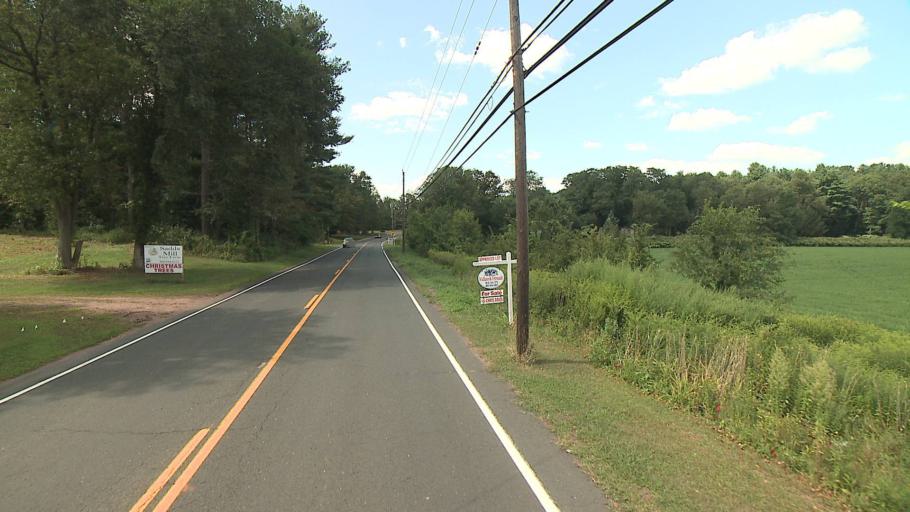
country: US
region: Connecticut
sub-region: Tolland County
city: Ellington
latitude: 41.9076
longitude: -72.4808
